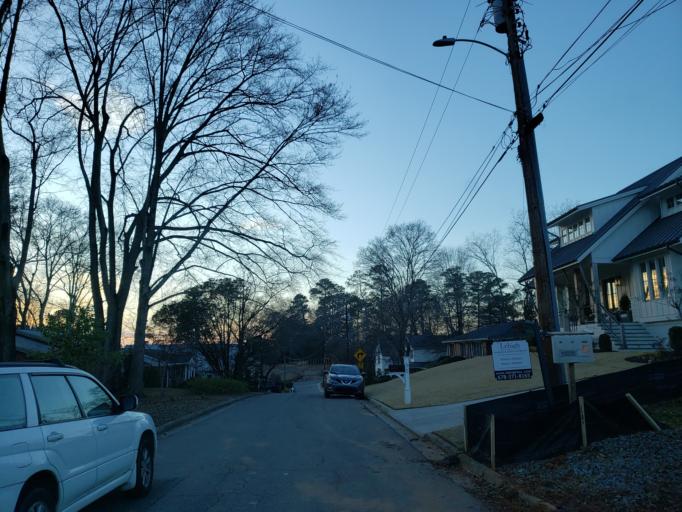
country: US
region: Georgia
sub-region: Fulton County
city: Roswell
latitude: 34.0298
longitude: -84.3630
